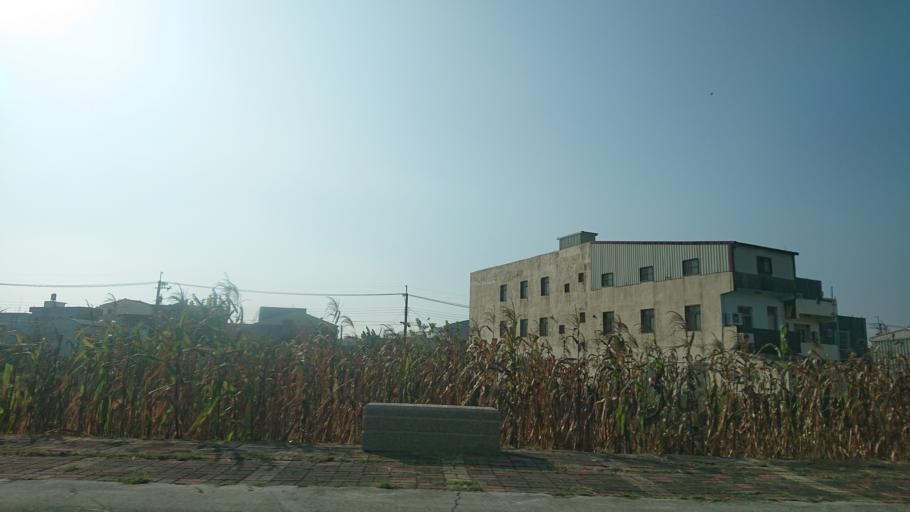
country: TW
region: Taiwan
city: Xinying
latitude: 23.3382
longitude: 120.2505
